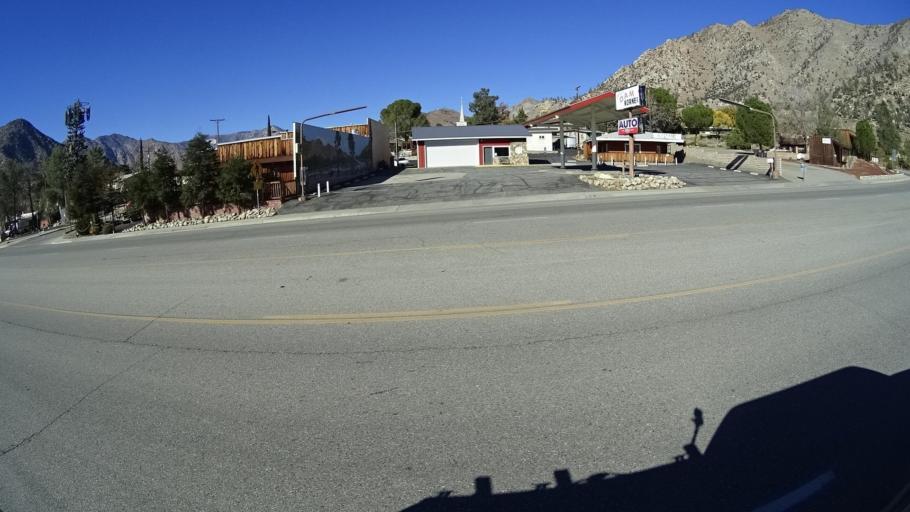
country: US
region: California
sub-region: Kern County
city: Kernville
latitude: 35.7537
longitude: -118.4208
